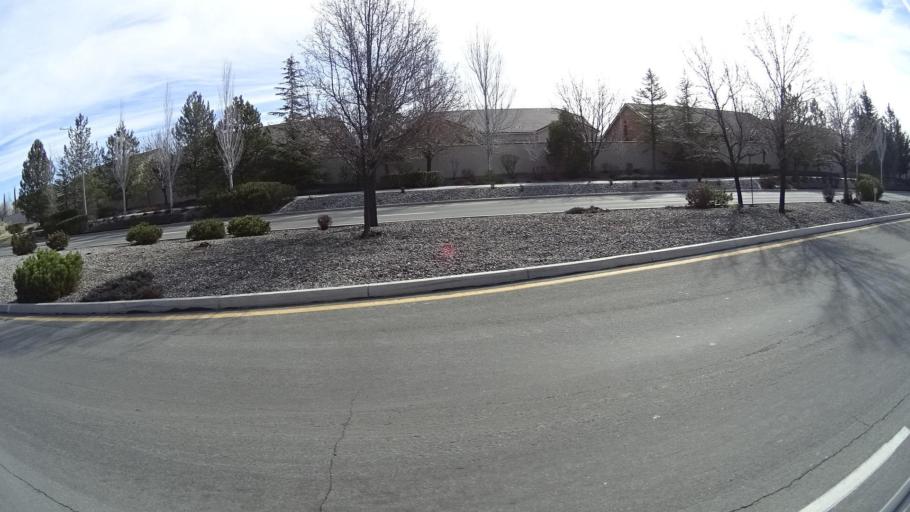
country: US
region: Nevada
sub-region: Washoe County
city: Sun Valley
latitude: 39.5831
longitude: -119.7244
